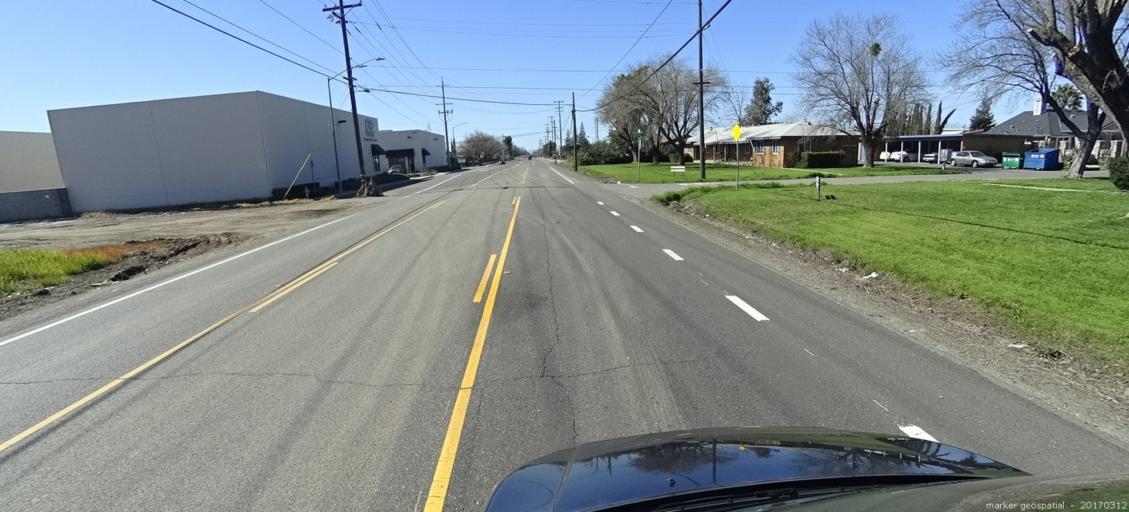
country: US
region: California
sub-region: Sacramento County
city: Rio Linda
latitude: 38.6472
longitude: -121.4182
